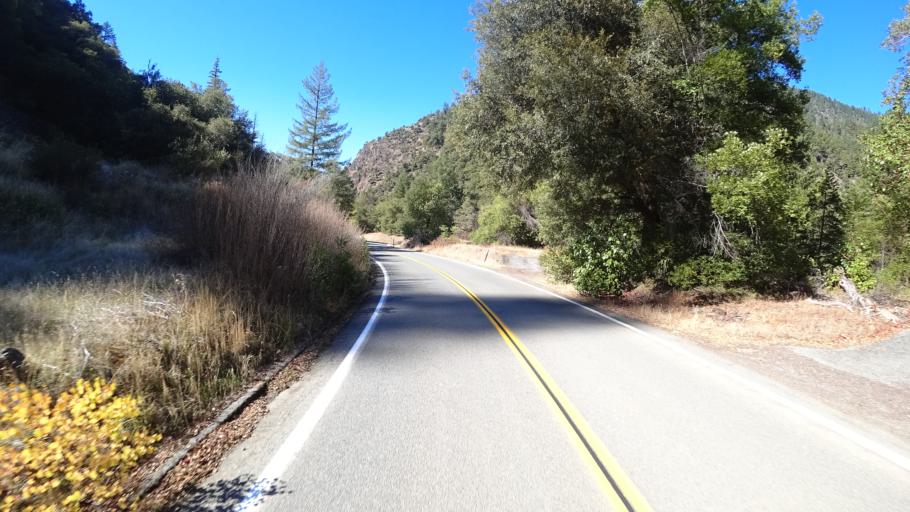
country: US
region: California
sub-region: Siskiyou County
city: Happy Camp
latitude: 41.3757
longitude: -123.4217
